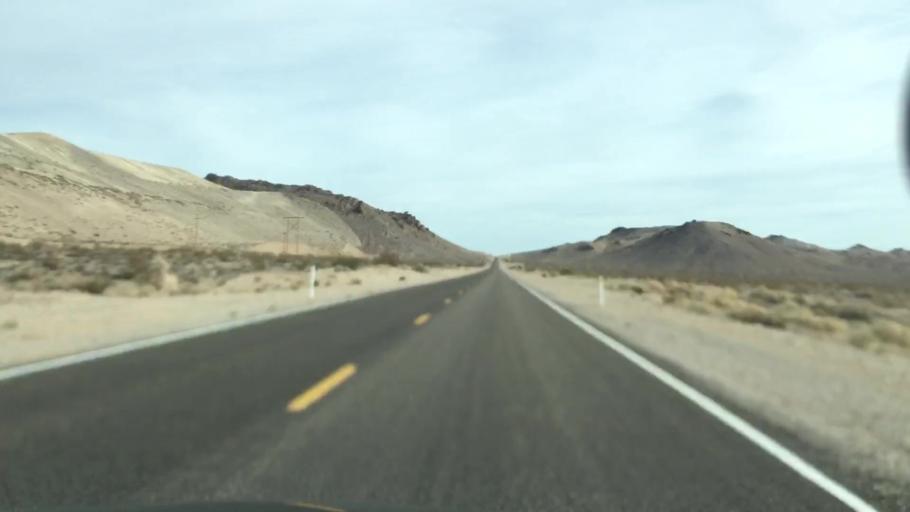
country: US
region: Nevada
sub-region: Nye County
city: Beatty
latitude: 36.8890
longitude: -116.8075
